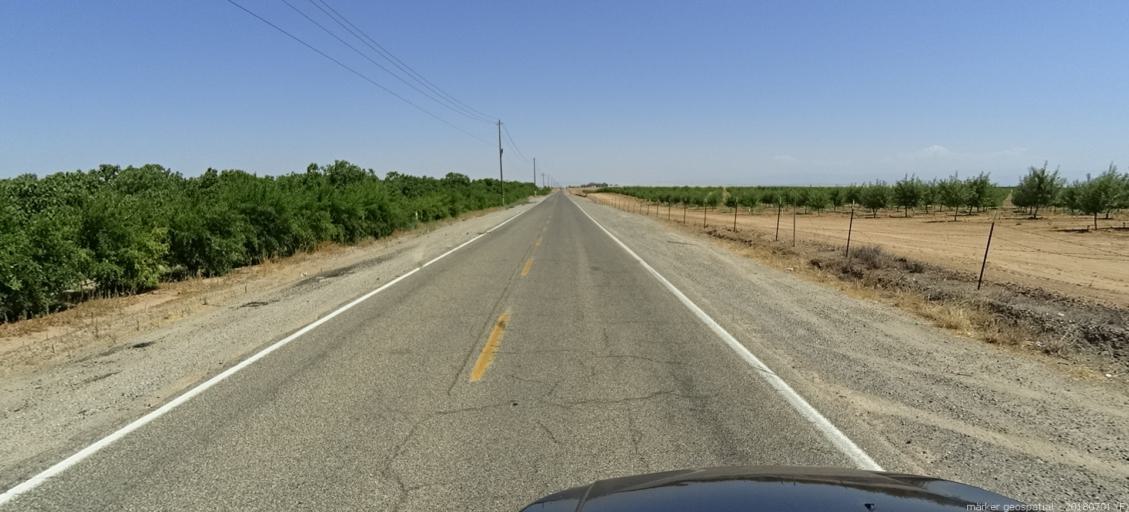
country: US
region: California
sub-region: Madera County
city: Madera Acres
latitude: 37.0067
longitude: -120.0287
